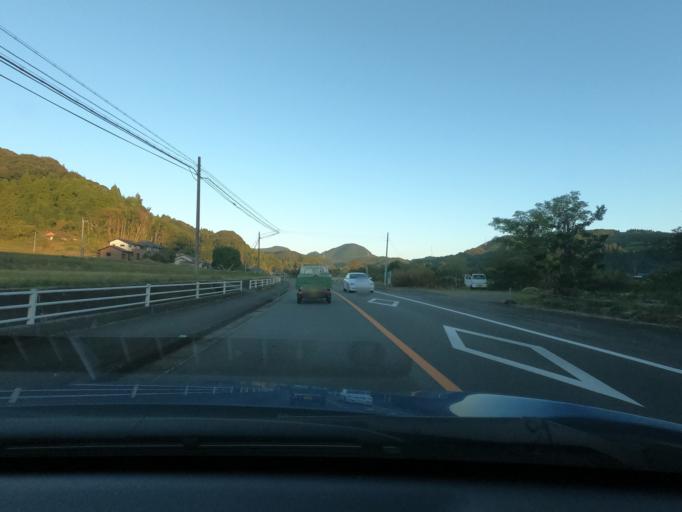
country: JP
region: Kagoshima
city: Satsumasendai
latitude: 31.7919
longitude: 130.4530
